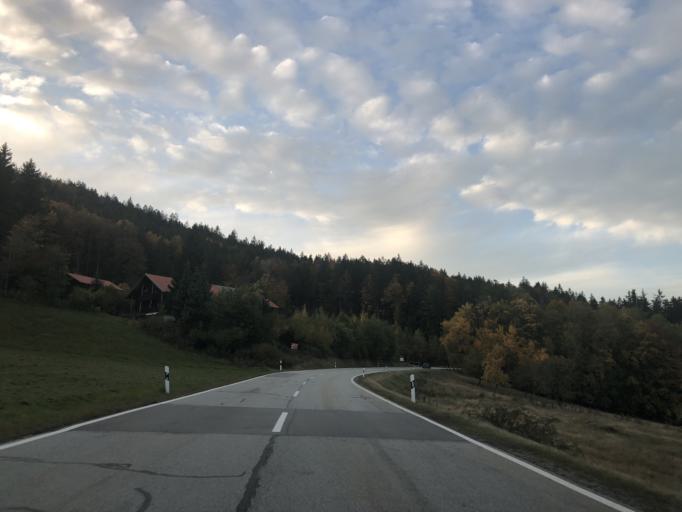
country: DE
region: Bavaria
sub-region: Lower Bavaria
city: Langdorf
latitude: 49.0304
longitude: 13.1220
